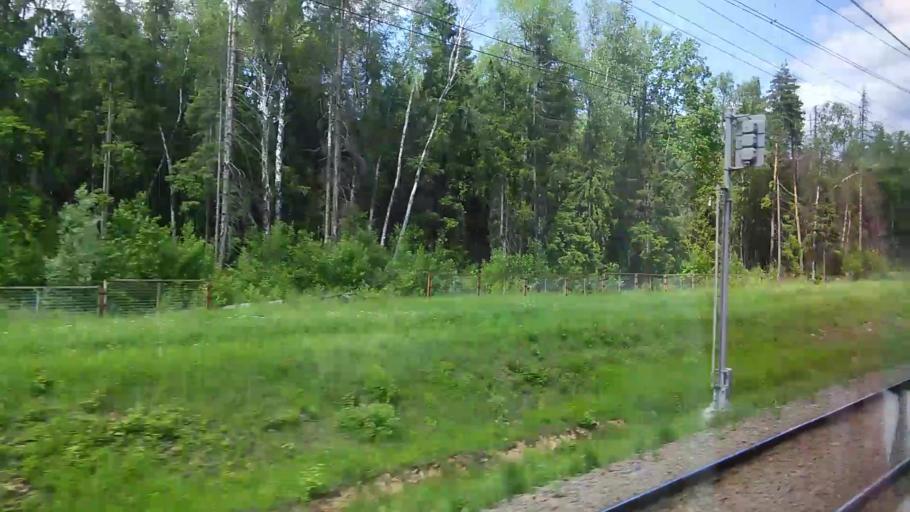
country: RU
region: Moskovskaya
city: Lobnya
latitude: 55.9899
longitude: 37.4713
